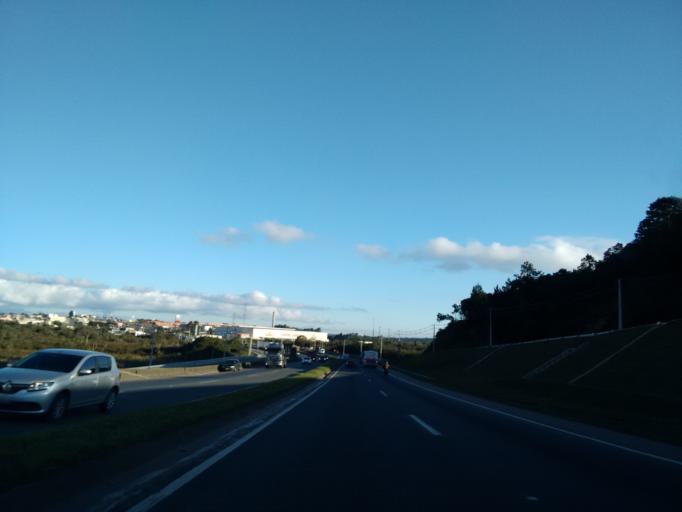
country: BR
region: Parana
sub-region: Sao Jose Dos Pinhais
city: Sao Jose dos Pinhais
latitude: -25.5949
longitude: -49.1732
